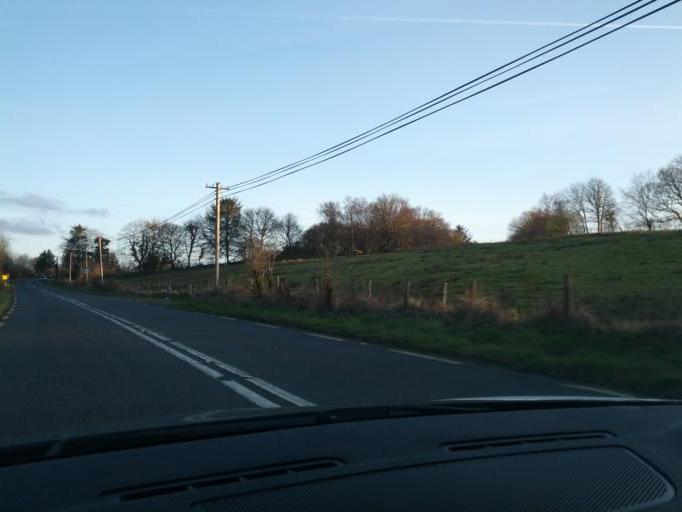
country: IE
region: Connaught
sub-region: Sligo
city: Tobercurry
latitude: 54.0836
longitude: -8.7042
